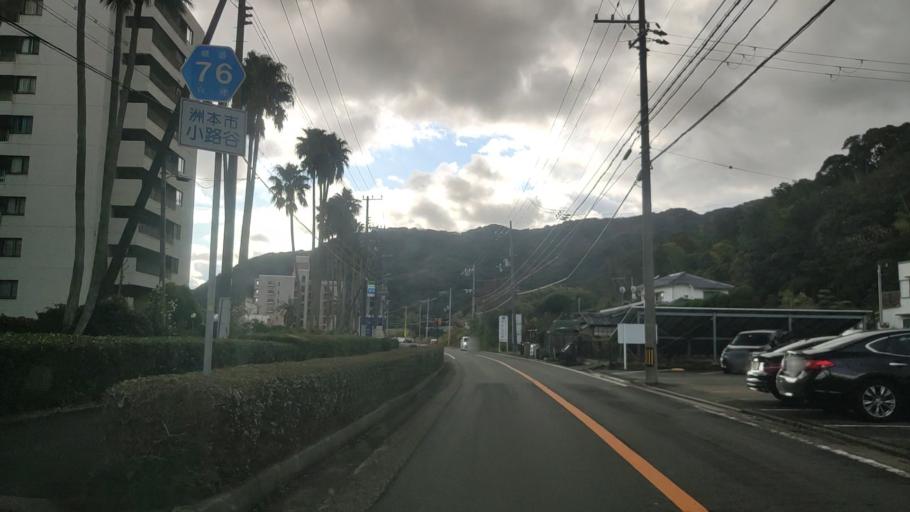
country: JP
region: Hyogo
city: Sumoto
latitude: 34.3295
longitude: 134.9119
